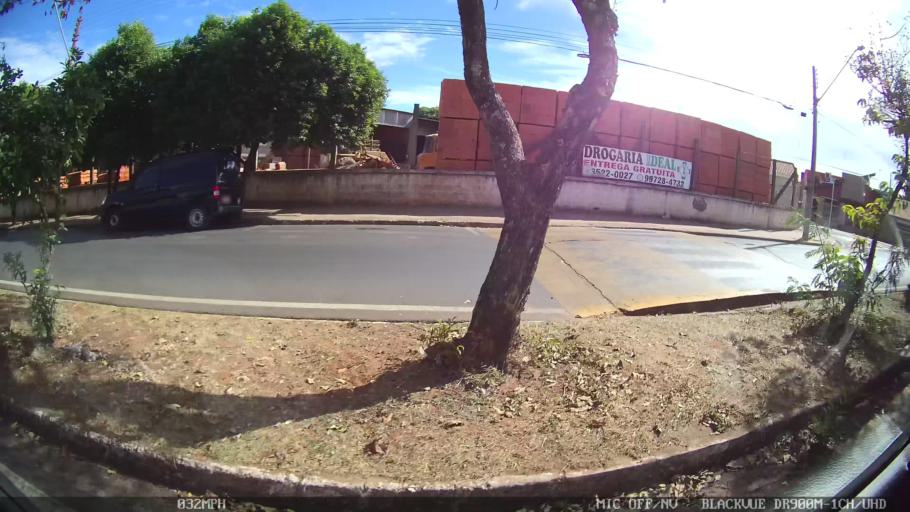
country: BR
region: Sao Paulo
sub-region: Catanduva
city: Catanduva
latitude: -21.1247
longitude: -48.9479
